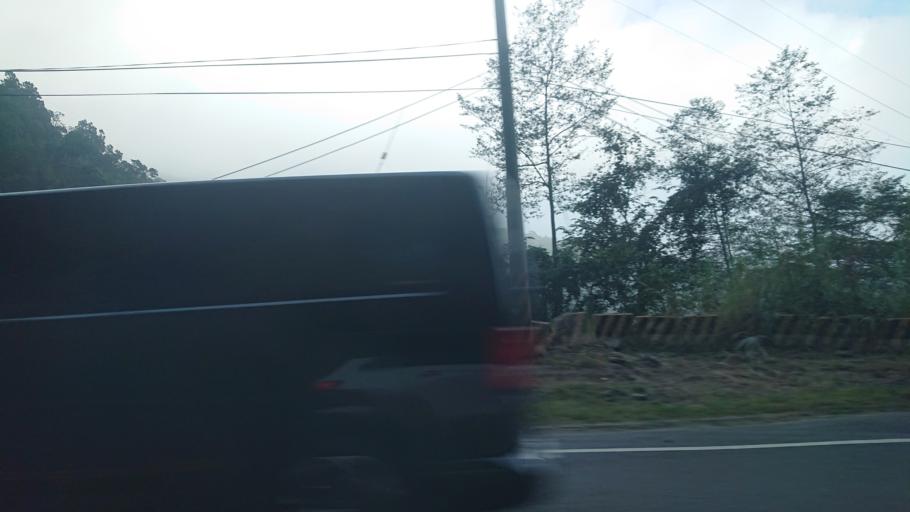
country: TW
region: Taiwan
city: Lugu
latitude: 23.4814
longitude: 120.7350
